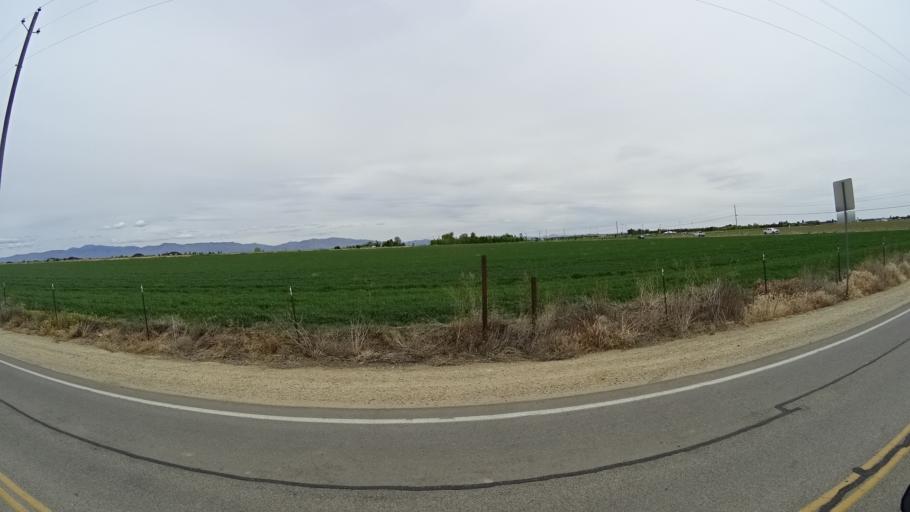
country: US
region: Idaho
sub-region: Ada County
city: Meridian
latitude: 43.5474
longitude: -116.3744
